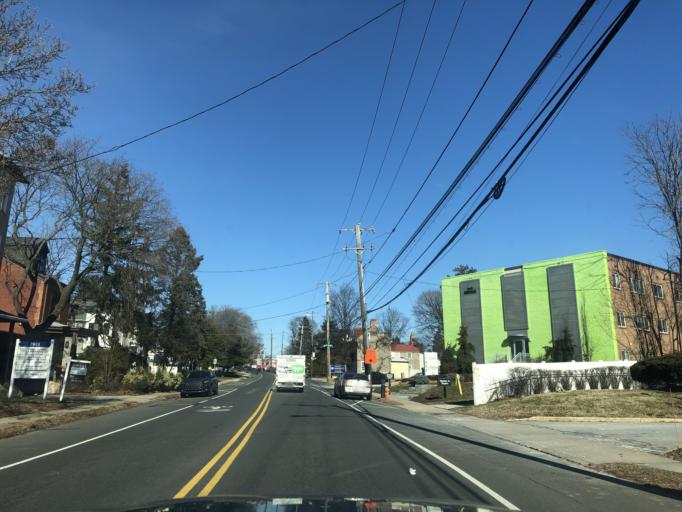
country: US
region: Pennsylvania
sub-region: Montgomery County
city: Bala-Cynwyd
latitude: 40.0546
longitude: -75.2360
